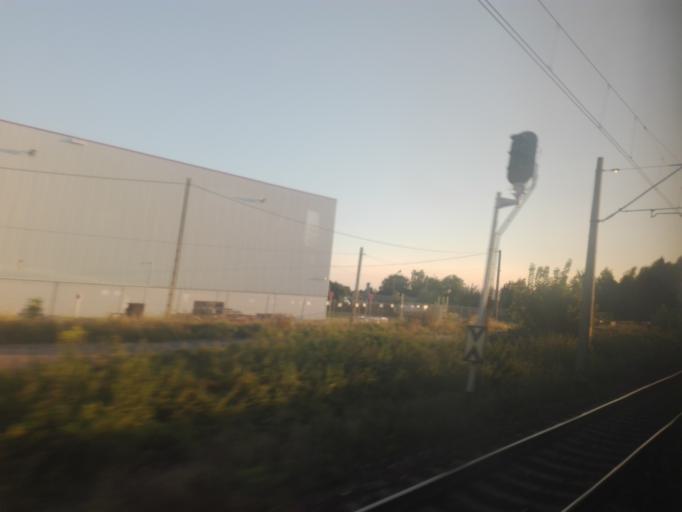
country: PL
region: Masovian Voivodeship
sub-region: Powiat warszawski zachodni
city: Ozarow Mazowiecki
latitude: 52.2083
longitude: 20.7660
